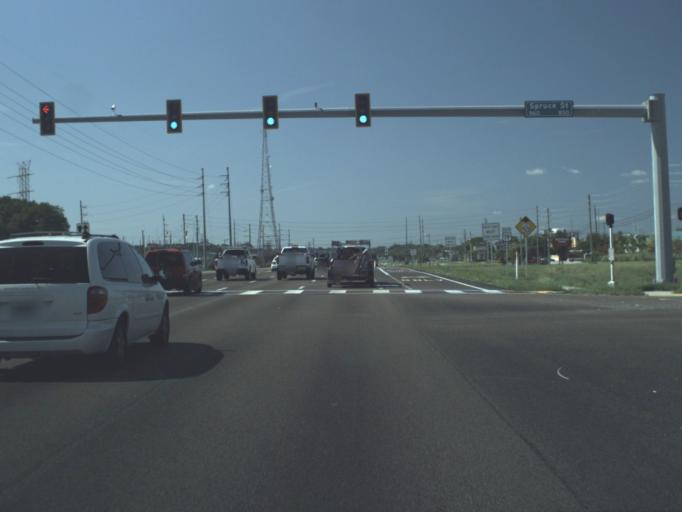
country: US
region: Florida
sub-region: Pinellas County
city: Tarpon Springs
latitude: 28.1528
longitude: -82.7406
